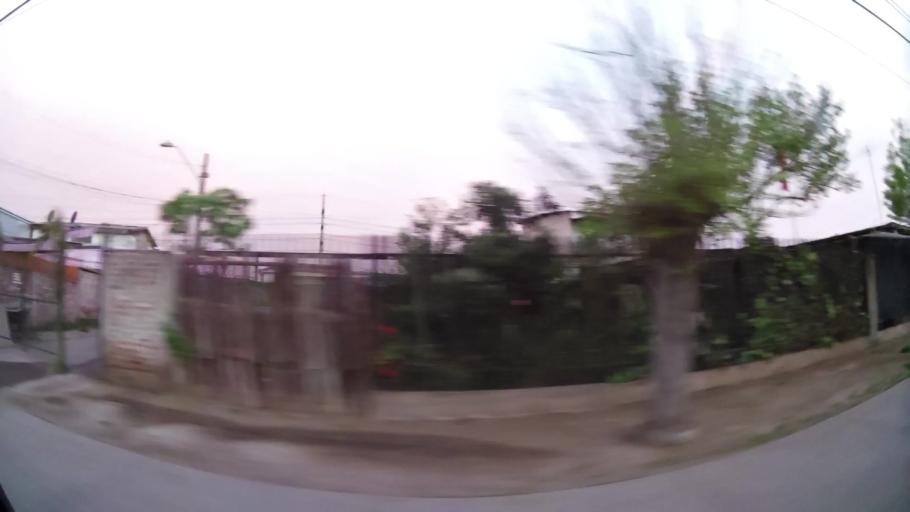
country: CL
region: Santiago Metropolitan
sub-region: Provincia de Santiago
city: Lo Prado
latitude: -33.4960
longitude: -70.7325
